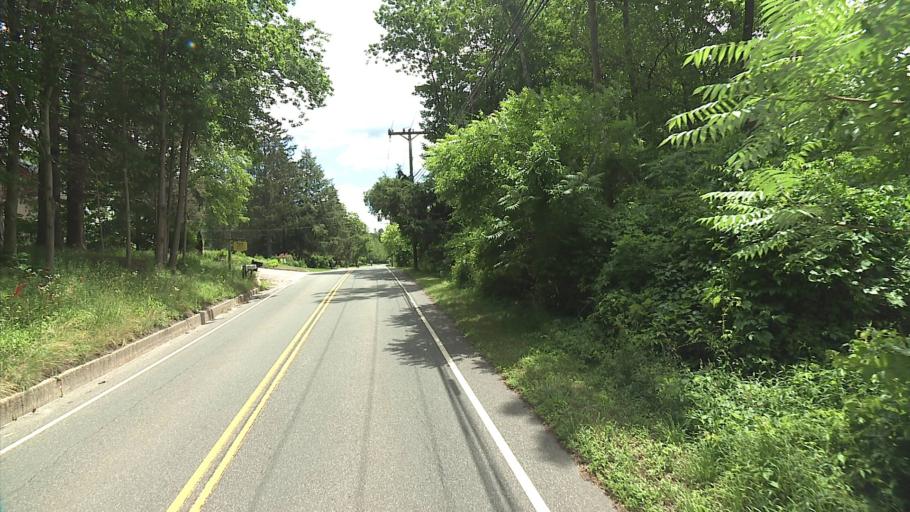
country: US
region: Connecticut
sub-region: Litchfield County
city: Canaan
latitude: 41.9327
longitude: -73.3868
